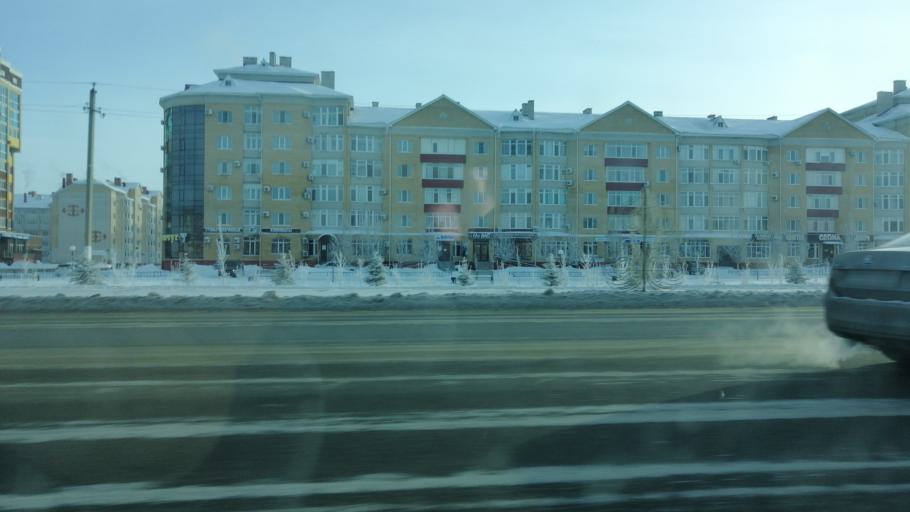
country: KZ
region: Aqtoebe
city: Aqtobe
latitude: 50.2839
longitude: 57.1412
